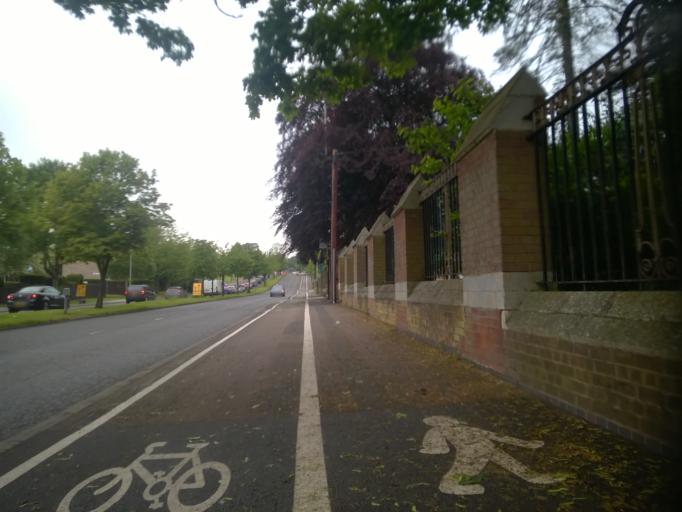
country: GB
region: England
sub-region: Leicestershire
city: Glenfield
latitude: 52.6510
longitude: -1.1712
